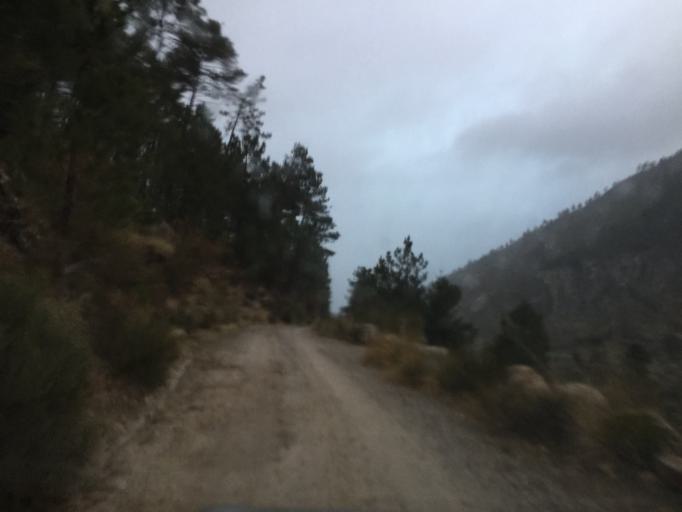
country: PT
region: Guarda
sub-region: Manteigas
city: Manteigas
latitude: 40.3689
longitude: -7.5527
